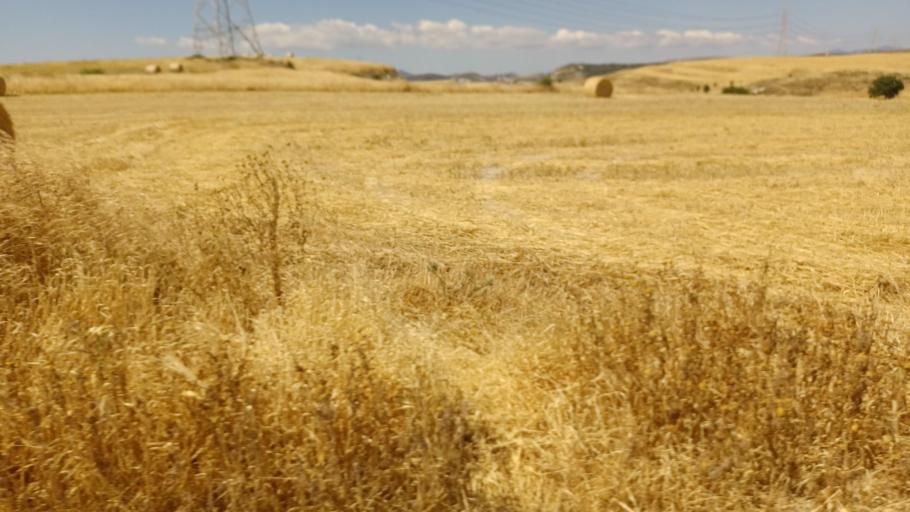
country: CY
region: Larnaka
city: Aradippou
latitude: 34.9942
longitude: 33.5474
